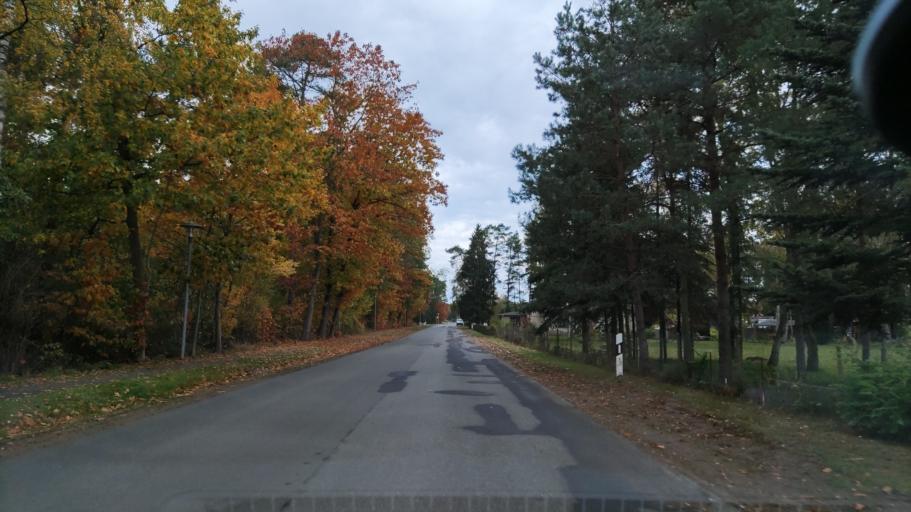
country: DE
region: Mecklenburg-Vorpommern
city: Boizenburg
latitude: 53.3714
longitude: 10.8584
